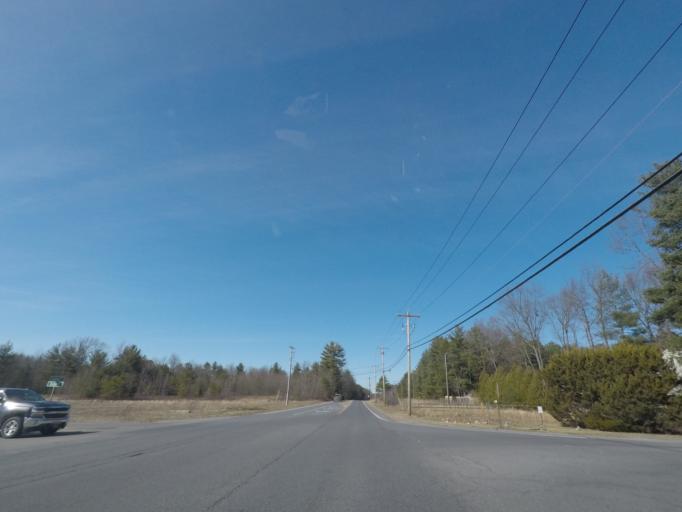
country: US
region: New York
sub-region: Saratoga County
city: Milton
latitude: 43.0490
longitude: -73.8505
